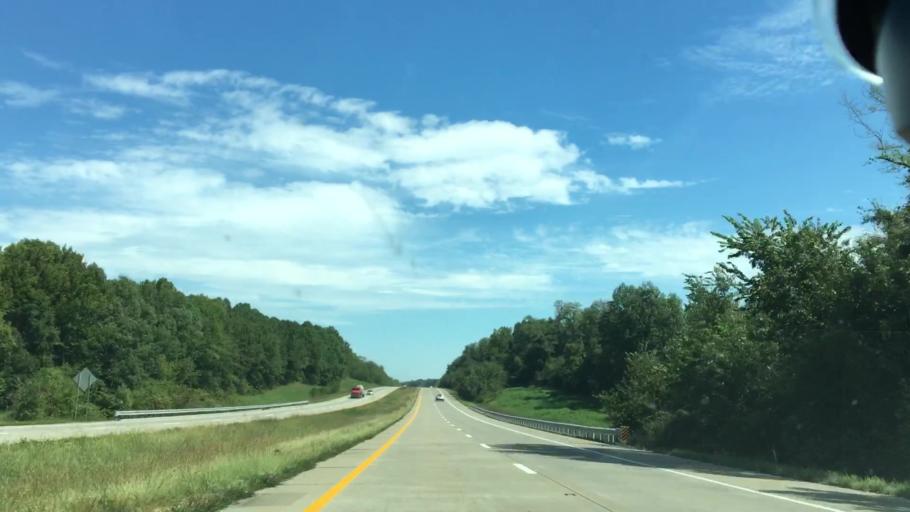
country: US
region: Indiana
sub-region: Warrick County
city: Newburgh
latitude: 37.7559
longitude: -87.3550
